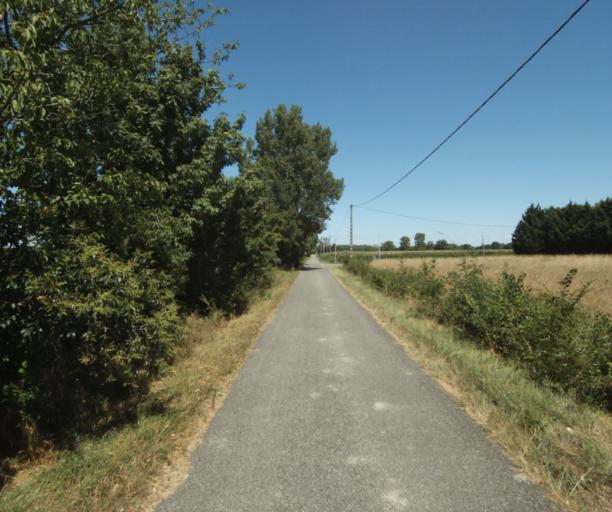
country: FR
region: Midi-Pyrenees
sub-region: Departement de la Haute-Garonne
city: Revel
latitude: 43.4889
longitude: 1.9568
